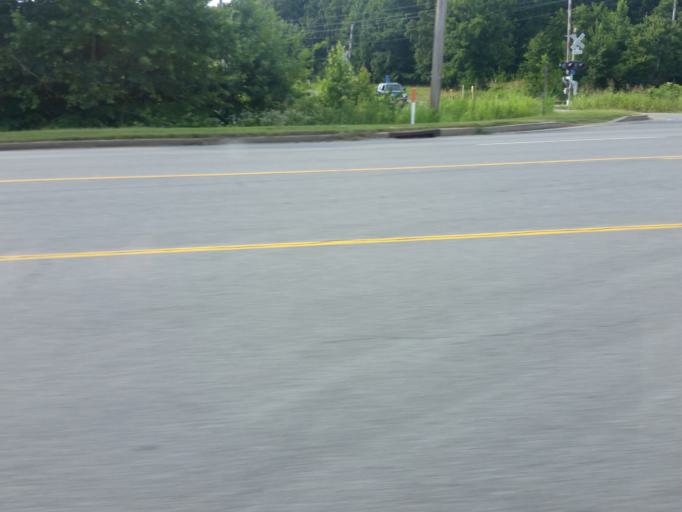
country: US
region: Tennessee
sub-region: Humphreys County
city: New Johnsonville
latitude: 36.0208
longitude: -87.9675
